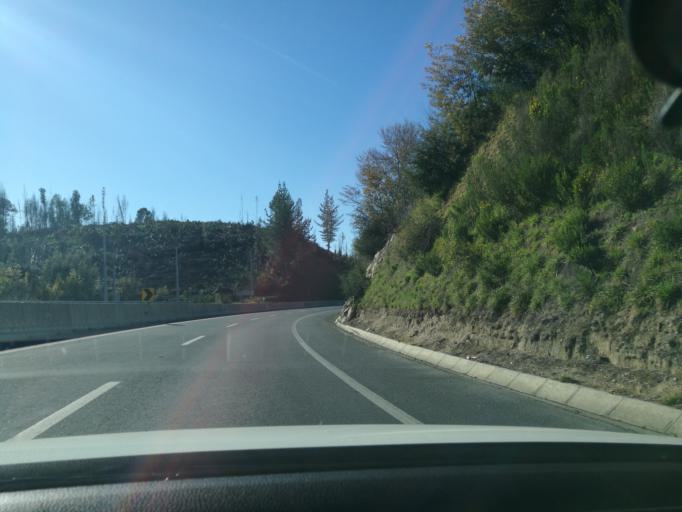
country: CL
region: Biobio
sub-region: Provincia de Concepcion
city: Penco
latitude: -36.8497
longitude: -72.9046
